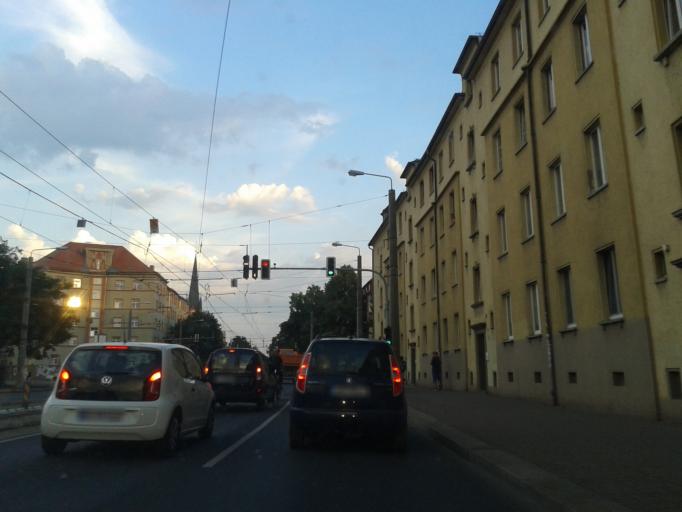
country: DE
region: Saxony
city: Dresden
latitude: 51.0760
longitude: 13.7332
